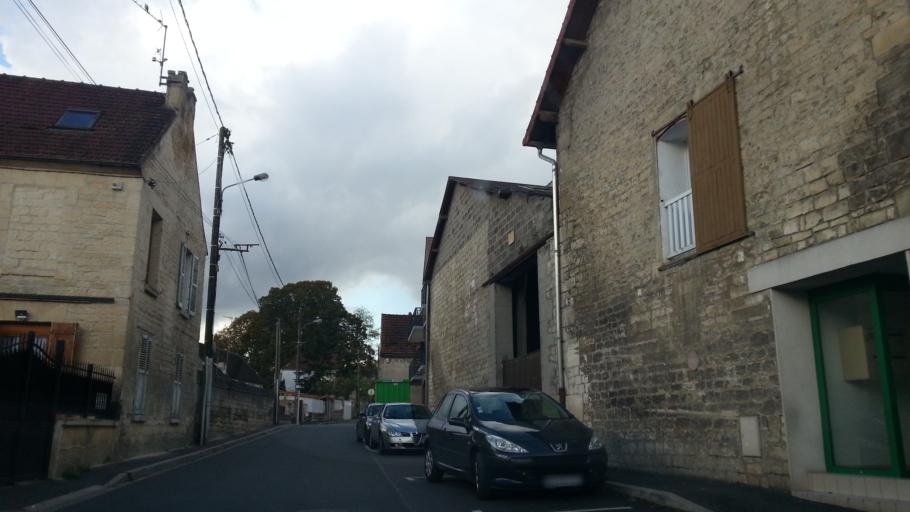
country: FR
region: Picardie
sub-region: Departement de l'Oise
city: Thiverny
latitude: 49.2575
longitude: 2.4000
